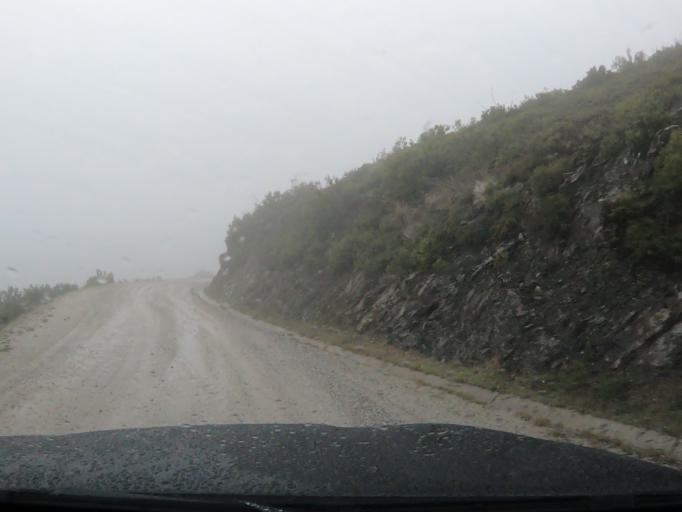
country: PT
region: Vila Real
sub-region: Vila Real
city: Vila Real
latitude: 41.3258
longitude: -7.8601
